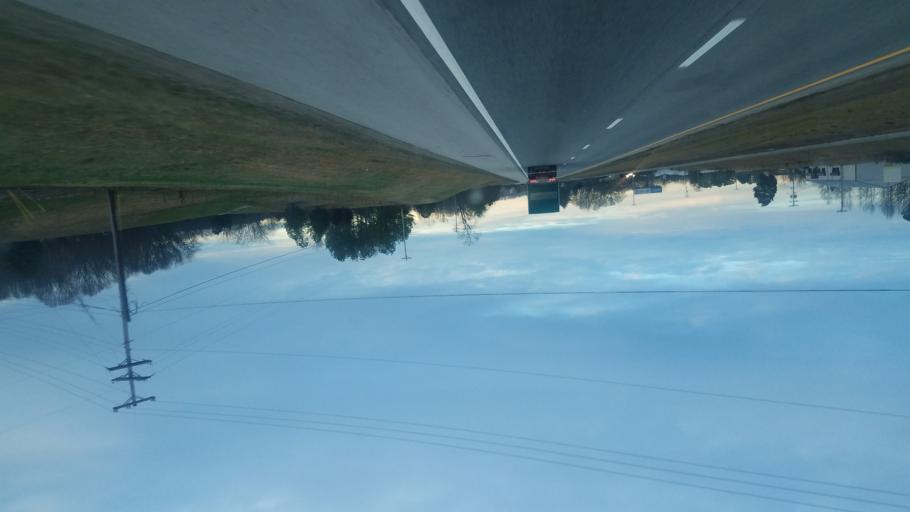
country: US
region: Tennessee
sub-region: Putnam County
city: Cookeville
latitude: 36.1142
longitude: -85.4955
